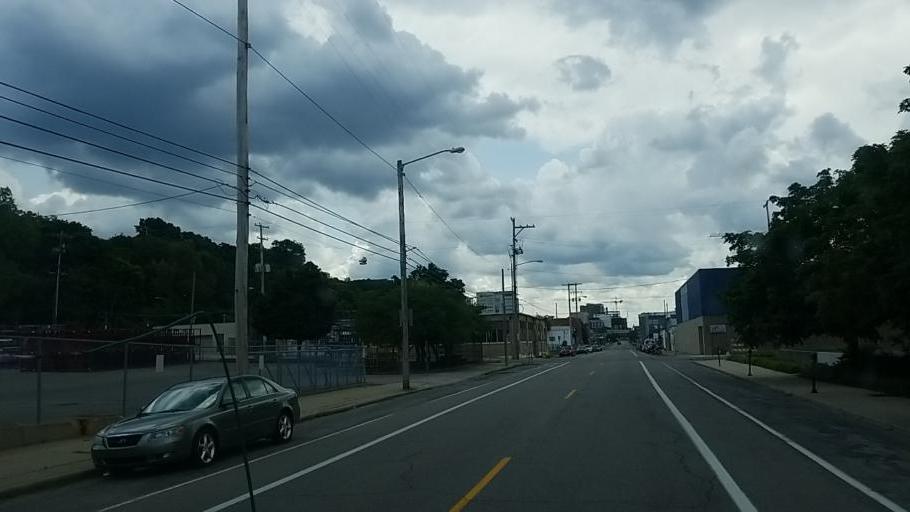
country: US
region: Michigan
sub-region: Kent County
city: Grand Rapids
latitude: 42.9789
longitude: -85.6704
